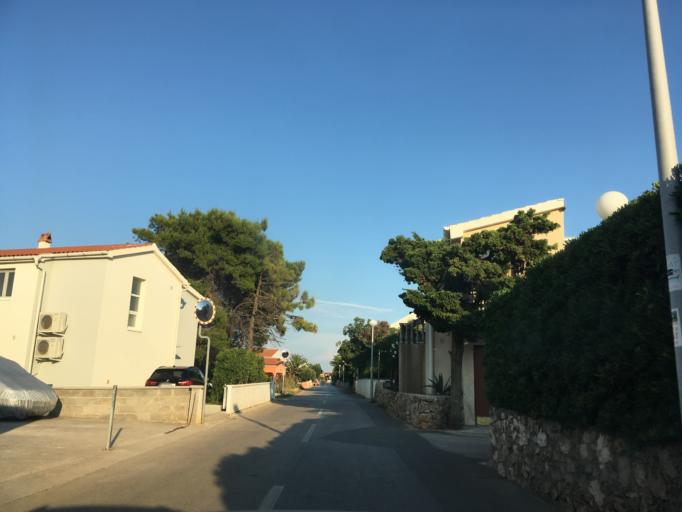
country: HR
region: Zadarska
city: Vir
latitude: 44.3078
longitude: 15.0836
